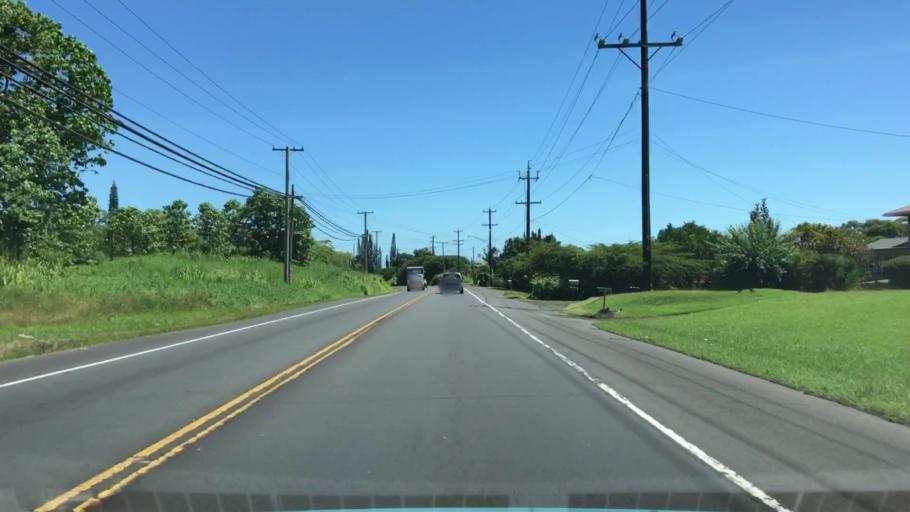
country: US
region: Hawaii
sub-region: Hawaii County
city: Kurtistown
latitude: 19.6060
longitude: -155.0503
